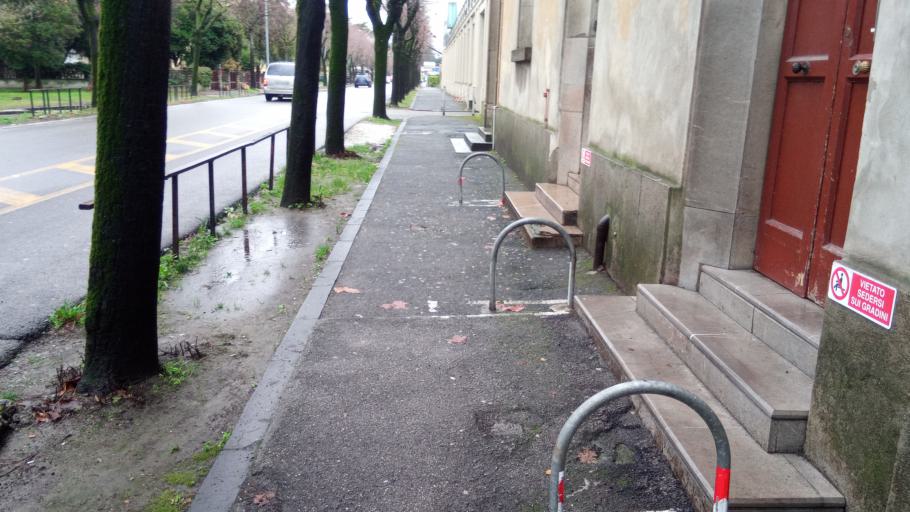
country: IT
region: Tuscany
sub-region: Province of Pisa
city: Pisa
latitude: 43.7192
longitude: 10.4141
